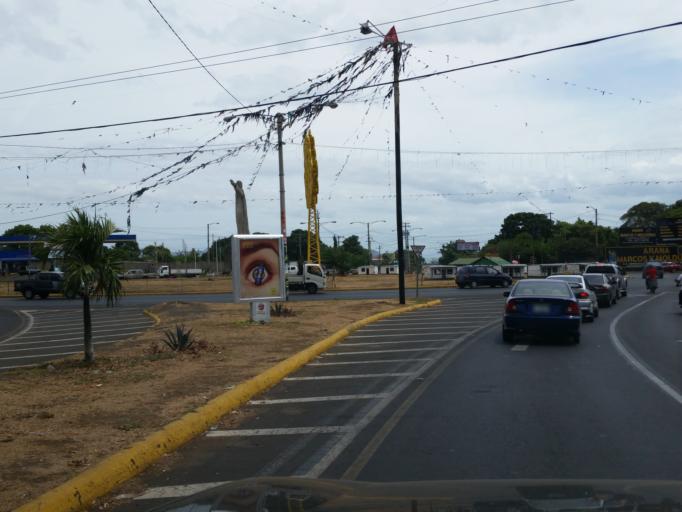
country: NI
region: Managua
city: Managua
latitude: 12.1320
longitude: -86.2573
